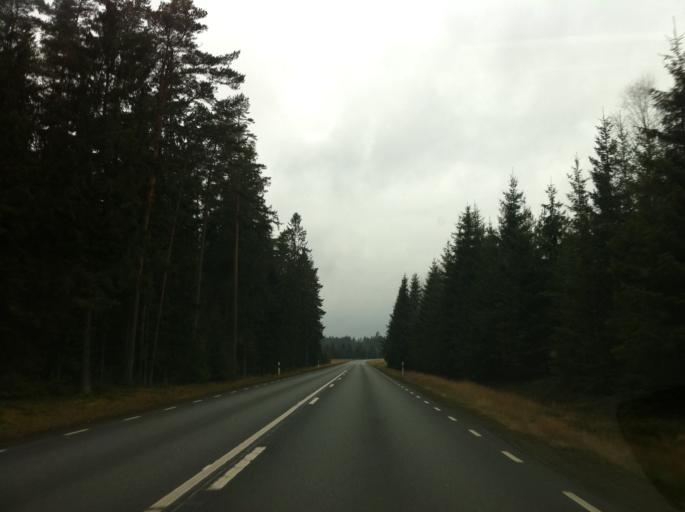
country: SE
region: Joenkoeping
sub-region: Savsjo Kommun
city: Saevsjoe
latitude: 57.3923
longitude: 14.7557
